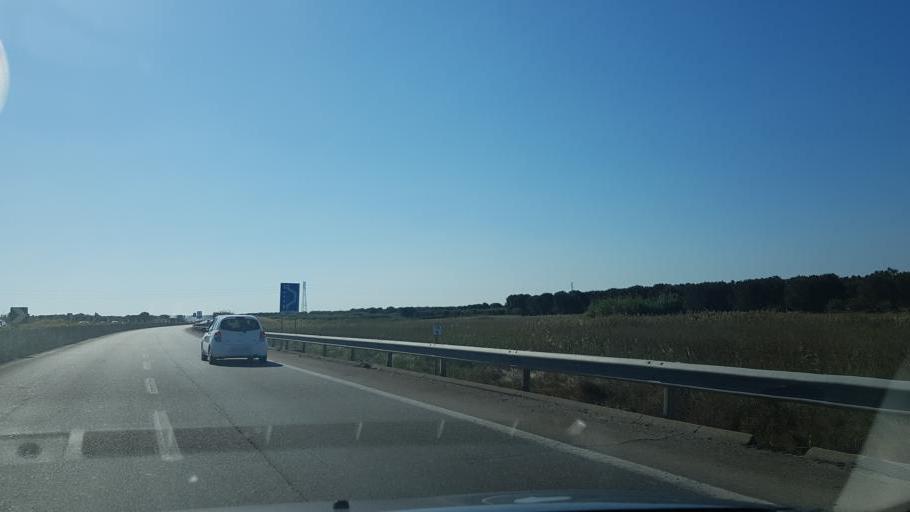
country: IT
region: Apulia
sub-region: Provincia di Brindisi
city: Tuturano
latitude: 40.5508
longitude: 17.9967
